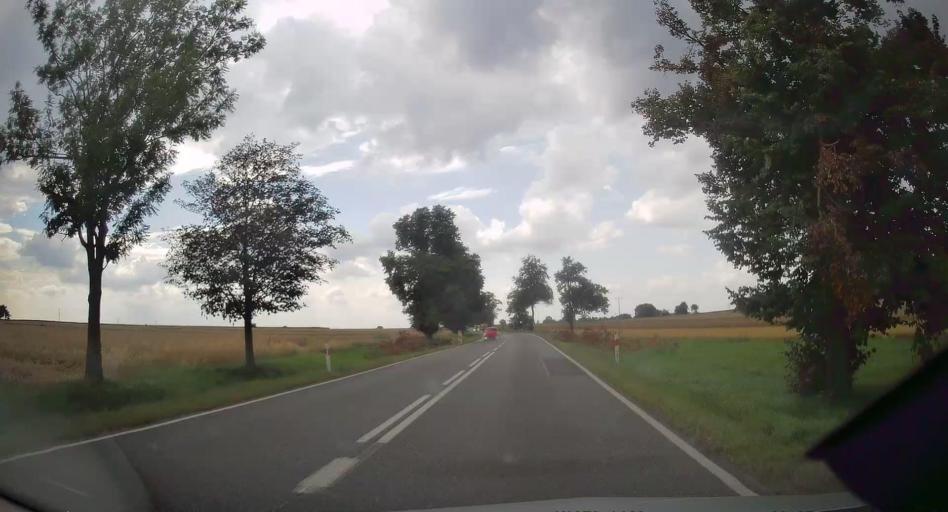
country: PL
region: Lodz Voivodeship
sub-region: Powiat skierniewicki
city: Gluchow
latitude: 51.7769
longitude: 20.1146
